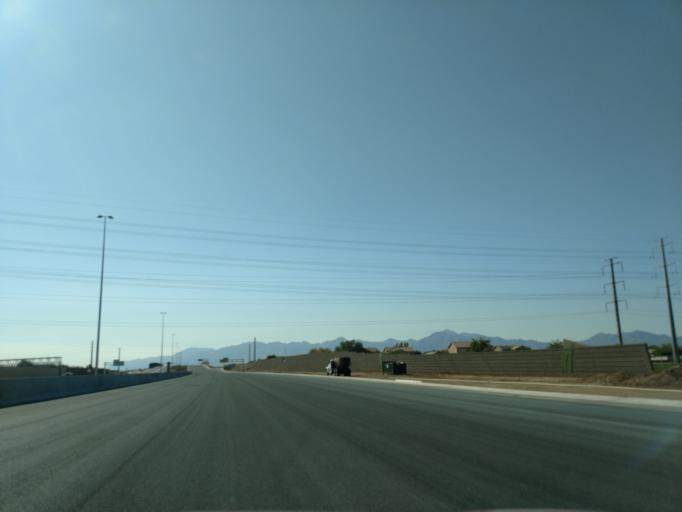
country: US
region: Arizona
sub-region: Maricopa County
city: Laveen
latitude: 33.4165
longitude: -112.1918
